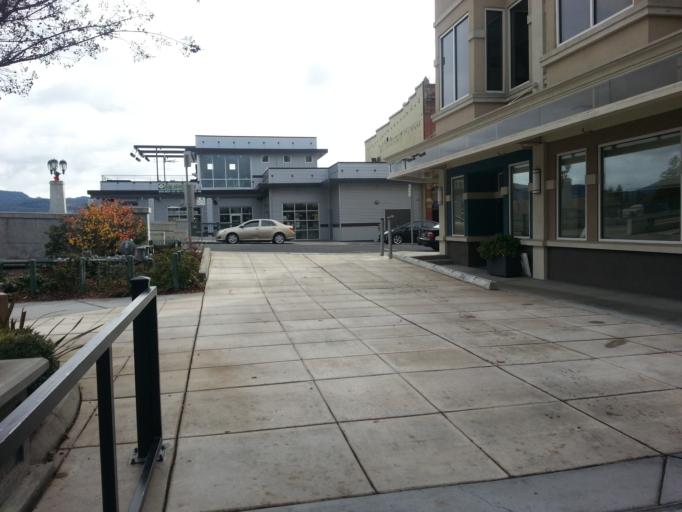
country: US
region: California
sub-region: Napa County
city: Napa
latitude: 38.2996
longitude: -122.2852
